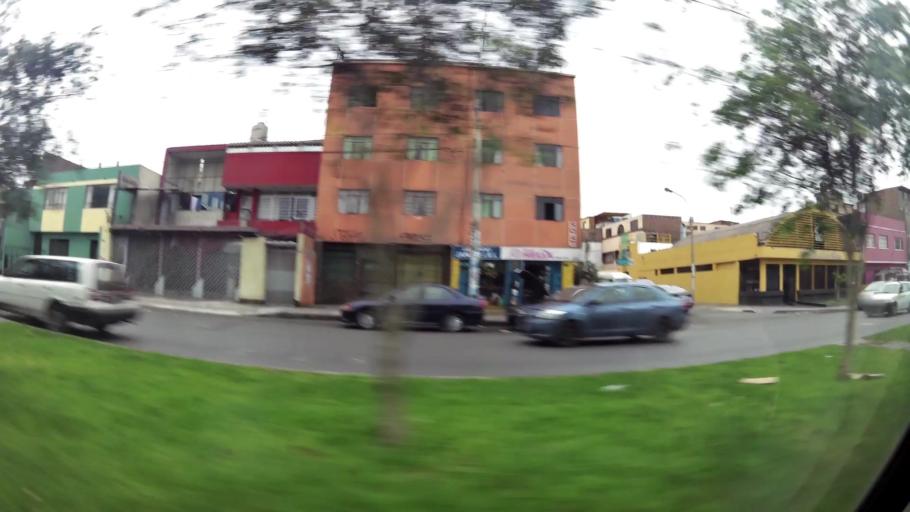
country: PE
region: Lima
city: Lima
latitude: -12.0534
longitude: -77.0613
